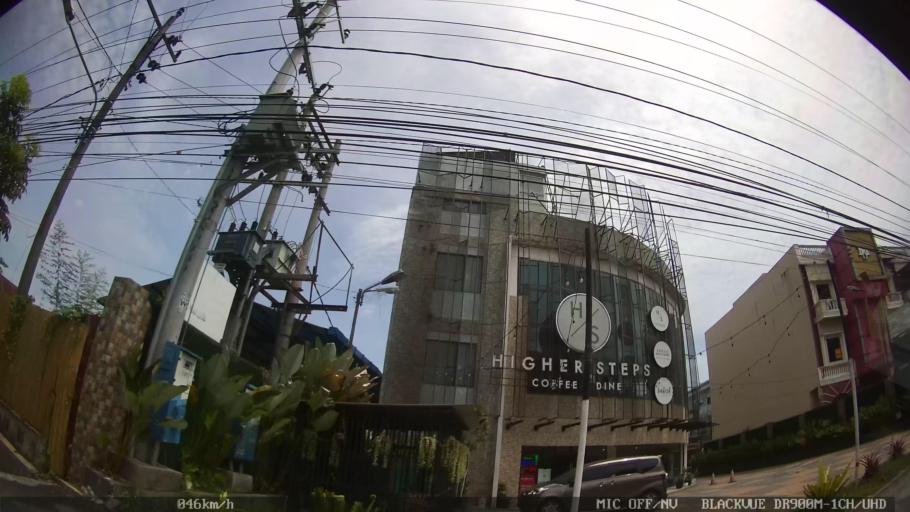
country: ID
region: North Sumatra
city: Sunggal
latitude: 3.5770
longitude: 98.6201
